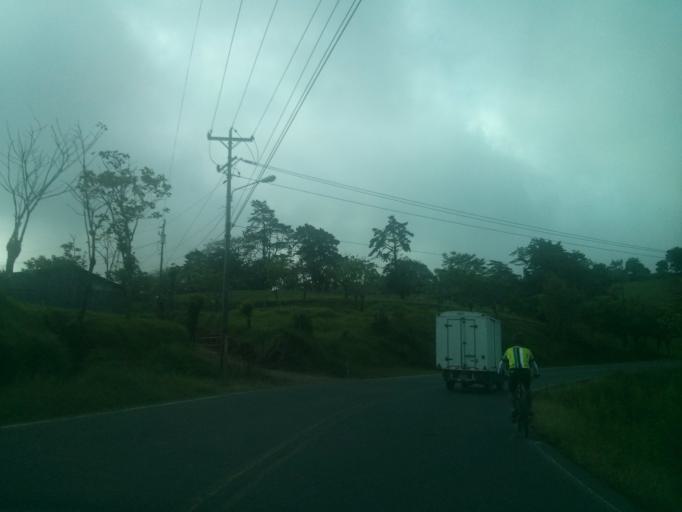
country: CR
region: Cartago
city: Paraiso
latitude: 9.8660
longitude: -83.8372
